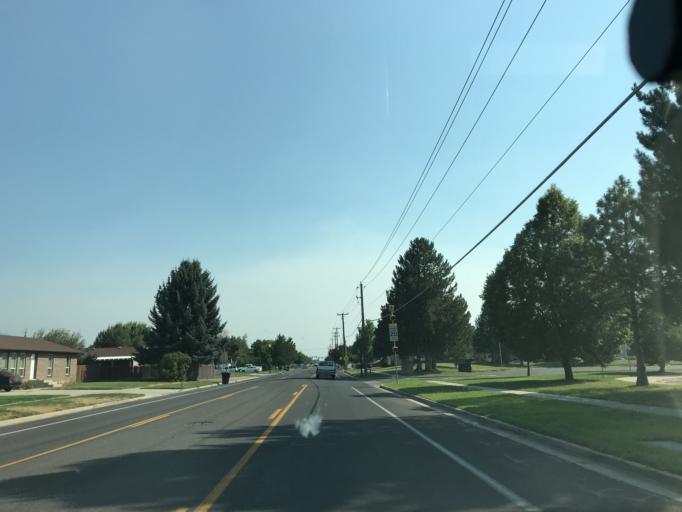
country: US
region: Utah
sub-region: Utah County
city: Orem
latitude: 40.3162
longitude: -111.6768
